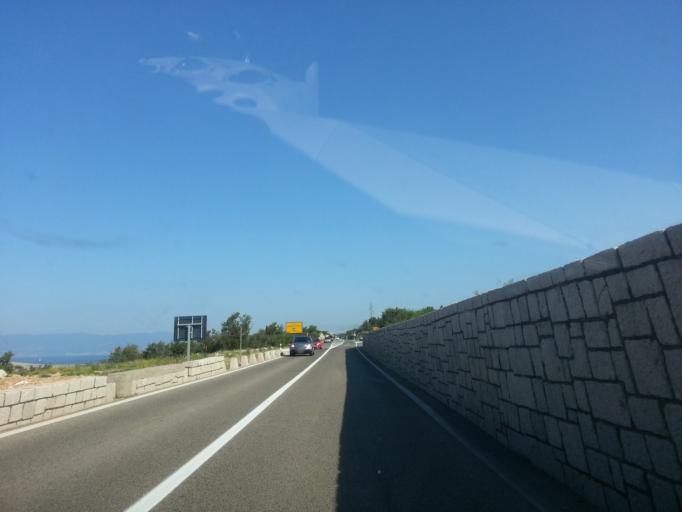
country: HR
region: Primorsko-Goranska
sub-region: Grad Crikvenica
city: Jadranovo
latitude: 45.2355
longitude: 14.6211
